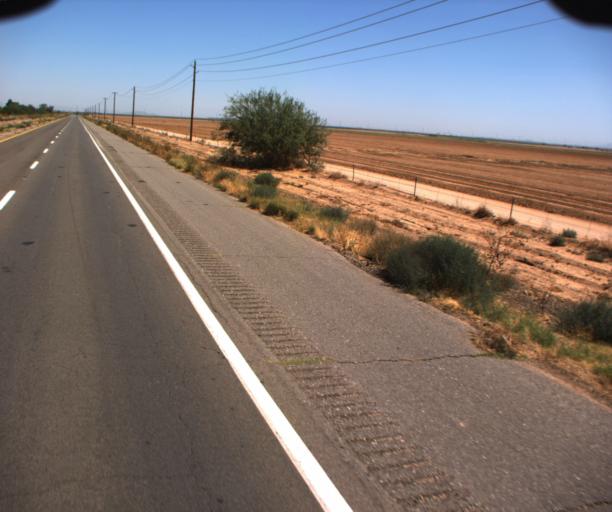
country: US
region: Arizona
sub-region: Pinal County
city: Maricopa
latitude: 32.9262
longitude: -112.0494
